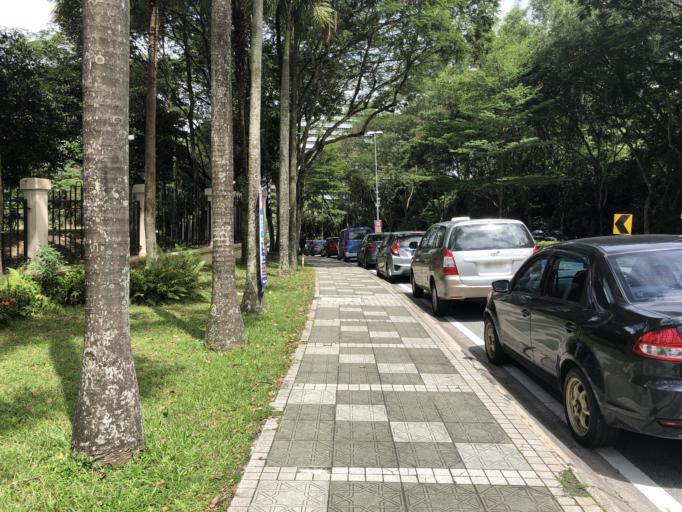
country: MY
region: Kuala Lumpur
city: Kuala Lumpur
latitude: 3.1719
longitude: 101.6725
